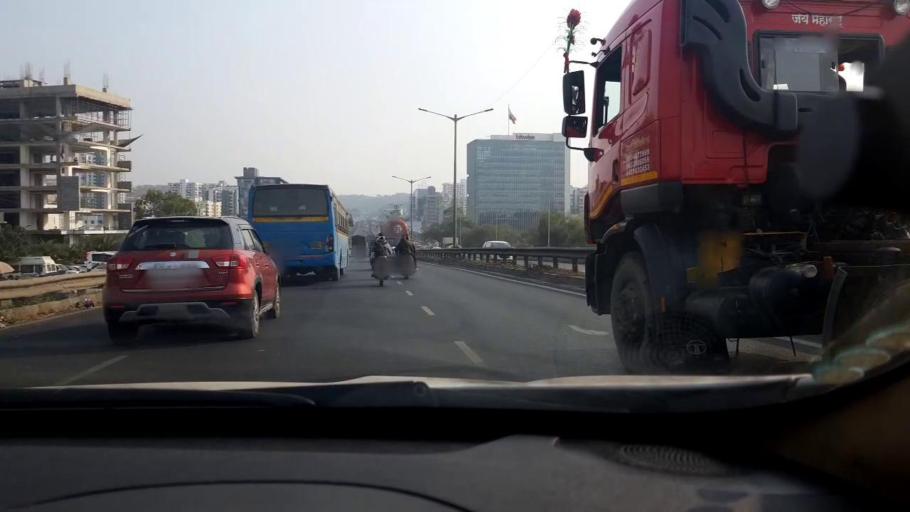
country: IN
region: Maharashtra
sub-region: Pune Division
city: Pimpri
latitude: 18.5605
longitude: 73.7690
